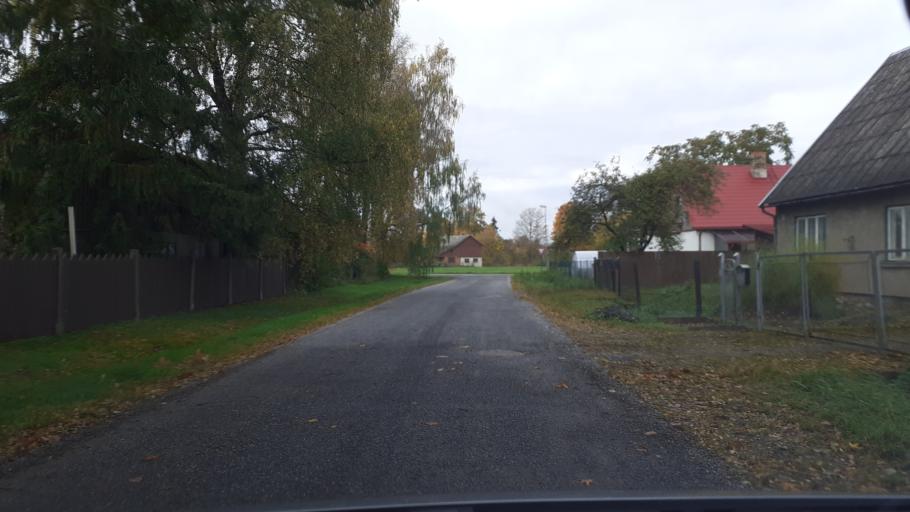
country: LV
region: Kuldigas Rajons
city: Kuldiga
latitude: 56.9729
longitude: 21.9889
